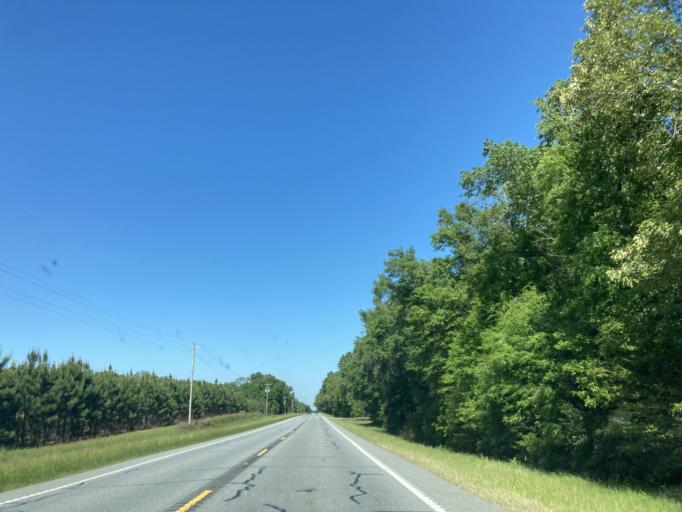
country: US
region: Georgia
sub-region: Baker County
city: Newton
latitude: 31.2767
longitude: -84.3801
